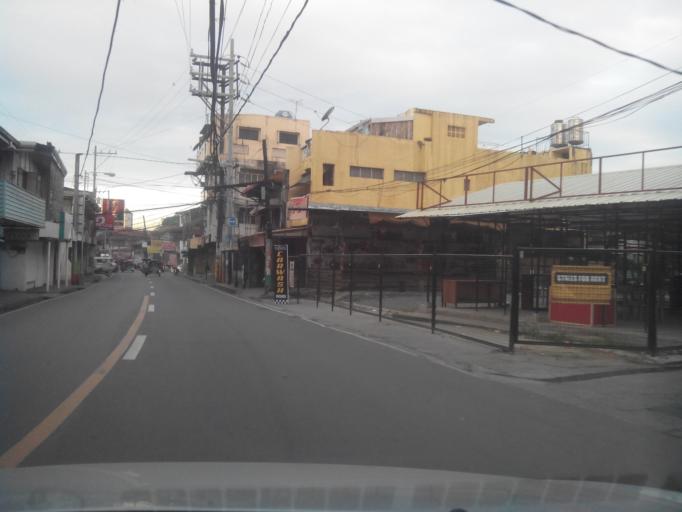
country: PH
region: Calabarzon
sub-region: Province of Rizal
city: Cainta
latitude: 14.5710
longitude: 121.1307
